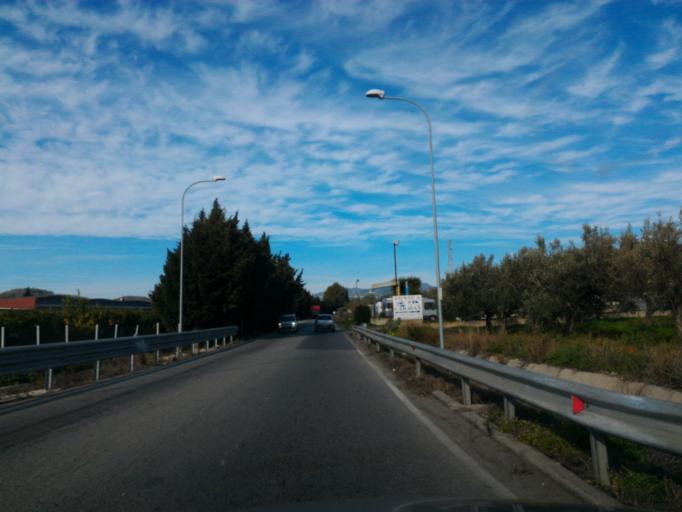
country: IT
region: Calabria
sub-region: Provincia di Catanzaro
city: Barone
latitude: 38.8586
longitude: 16.6745
